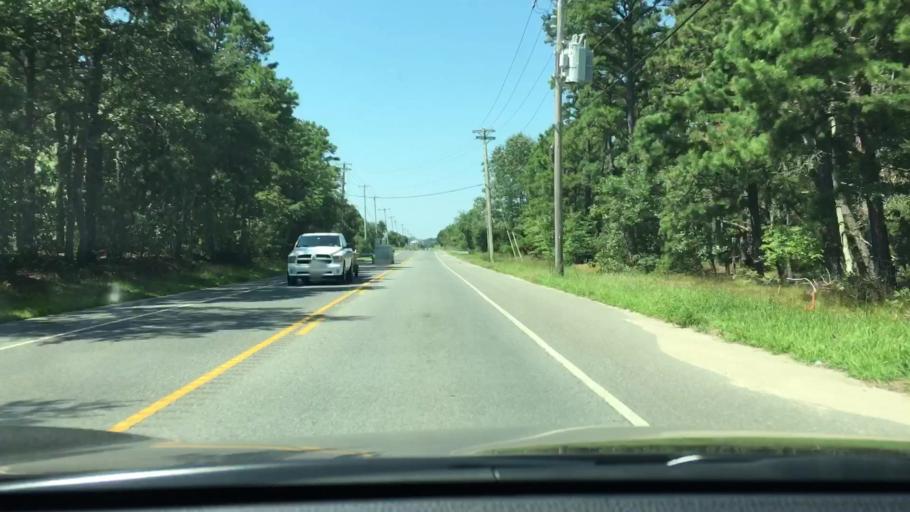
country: US
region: New Jersey
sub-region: Cumberland County
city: Laurel Lake
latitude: 39.2894
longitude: -74.9718
